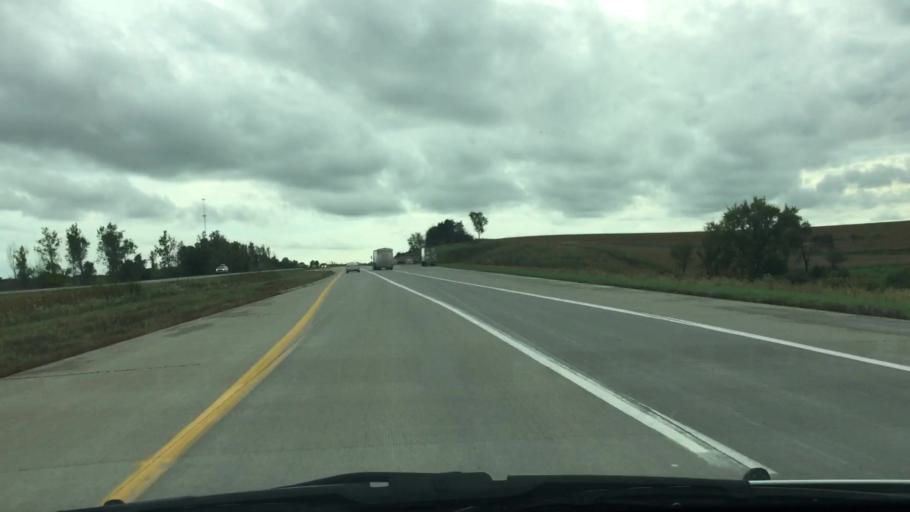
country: US
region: Iowa
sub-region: Warren County
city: Norwalk
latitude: 41.4485
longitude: -93.7801
